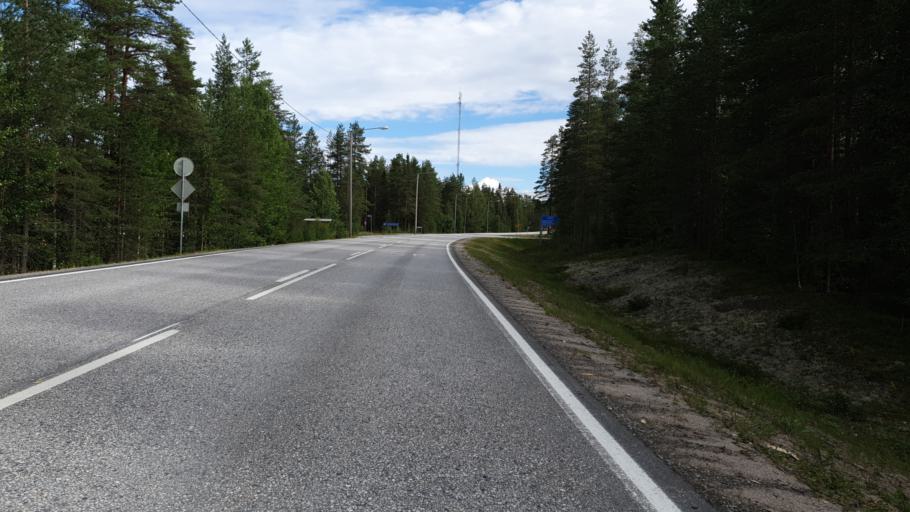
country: FI
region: Kainuu
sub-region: Kehys-Kainuu
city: Kuhmo
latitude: 64.5363
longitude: 29.9447
